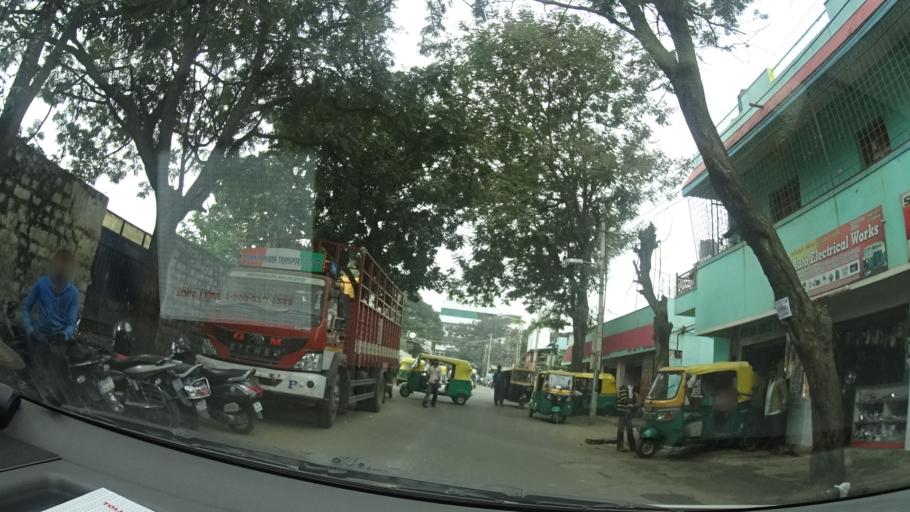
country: IN
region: Karnataka
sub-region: Bangalore Urban
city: Bangalore
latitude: 13.0345
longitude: 77.6237
